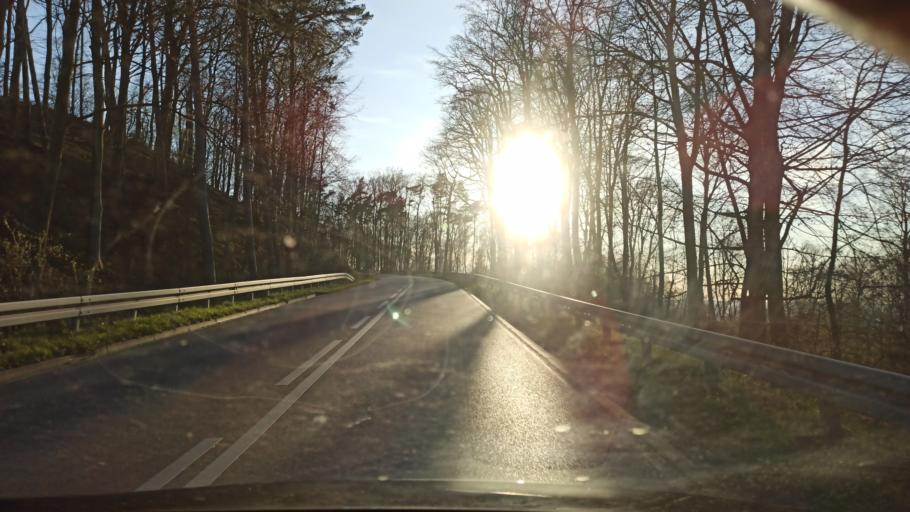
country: PL
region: Warmian-Masurian Voivodeship
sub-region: Powiat elblaski
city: Tolkmicko
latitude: 54.2918
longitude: 19.4715
